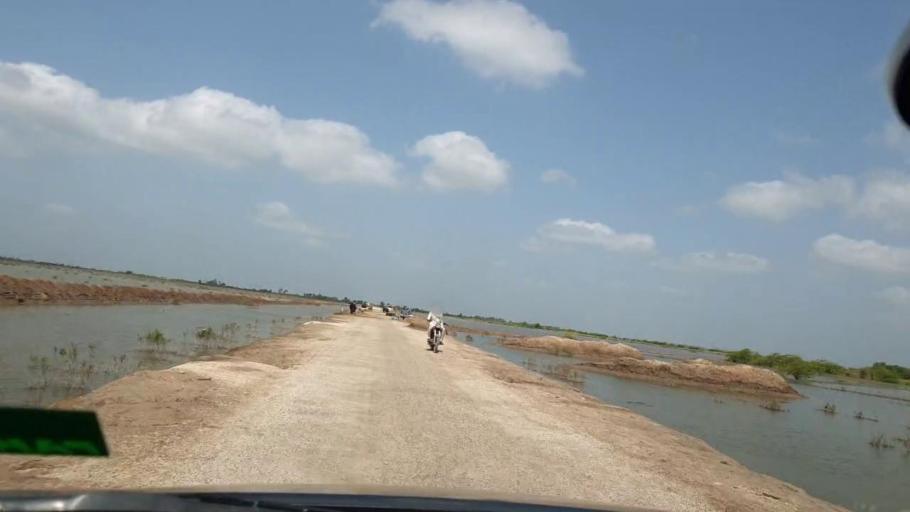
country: PK
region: Sindh
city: Kadhan
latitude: 24.5939
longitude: 69.1324
